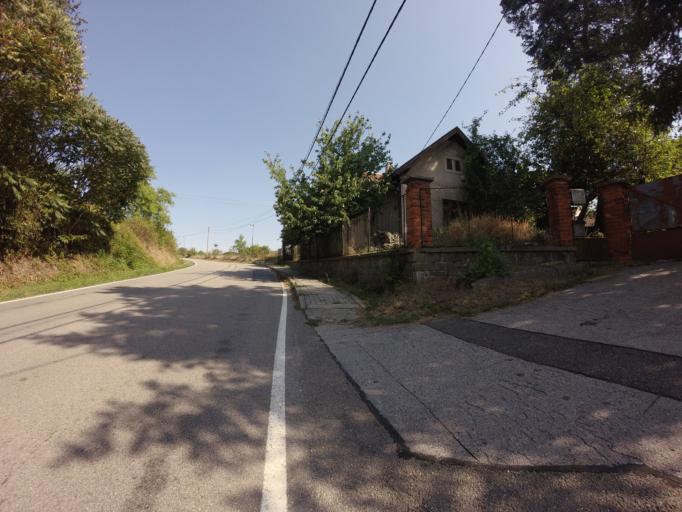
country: CZ
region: Central Bohemia
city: Kamenny Privoz
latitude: 49.8584
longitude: 14.5162
